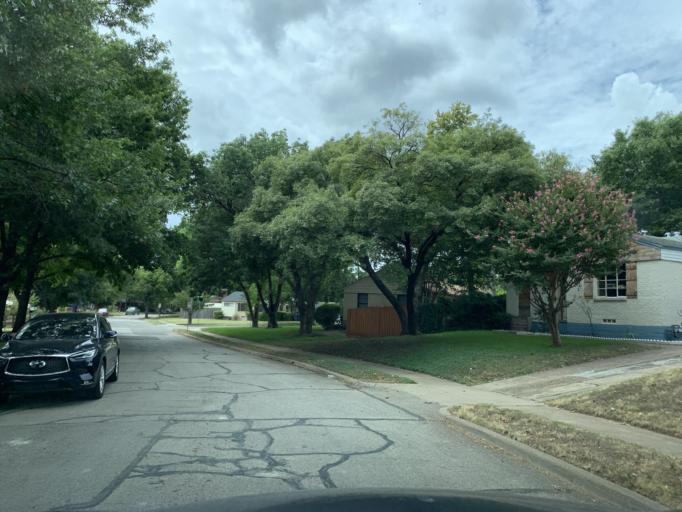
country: US
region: Texas
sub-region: Dallas County
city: Cockrell Hill
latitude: 32.7521
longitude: -96.8627
